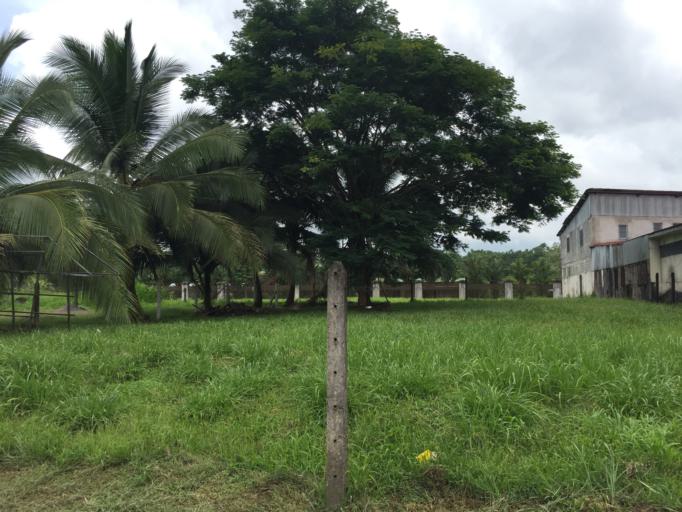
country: CR
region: Heredia
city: La Virgen
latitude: 10.4493
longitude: -84.0122
